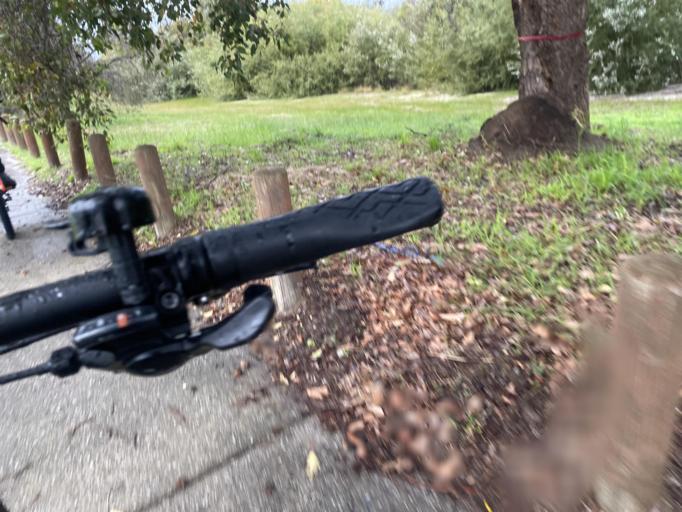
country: AU
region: Western Australia
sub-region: Canning
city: Queens Park
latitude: -31.9982
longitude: 115.9544
